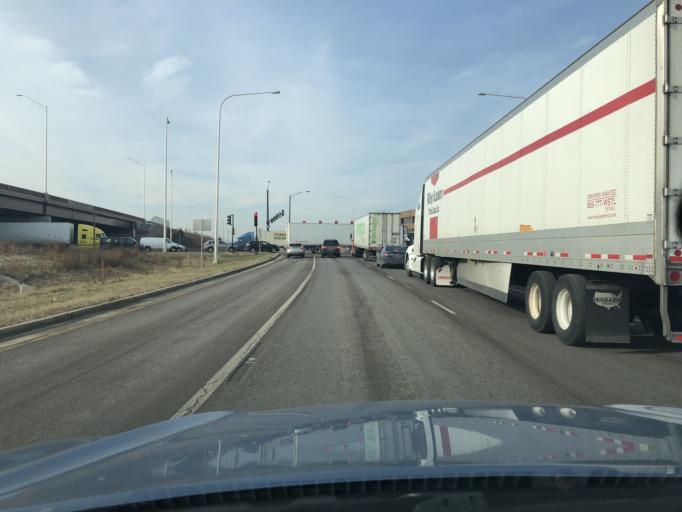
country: US
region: Illinois
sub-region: Cook County
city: Elk Grove Village
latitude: 41.9834
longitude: -87.9582
